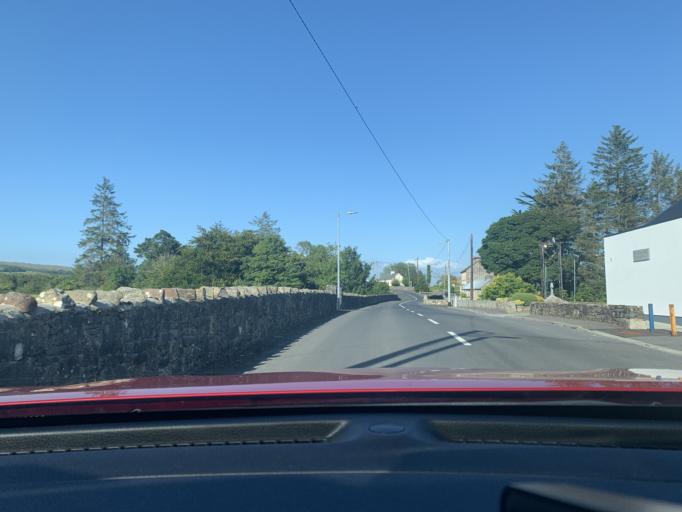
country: IE
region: Connaught
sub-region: Sligo
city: Tobercurry
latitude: 54.1010
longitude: -8.7773
